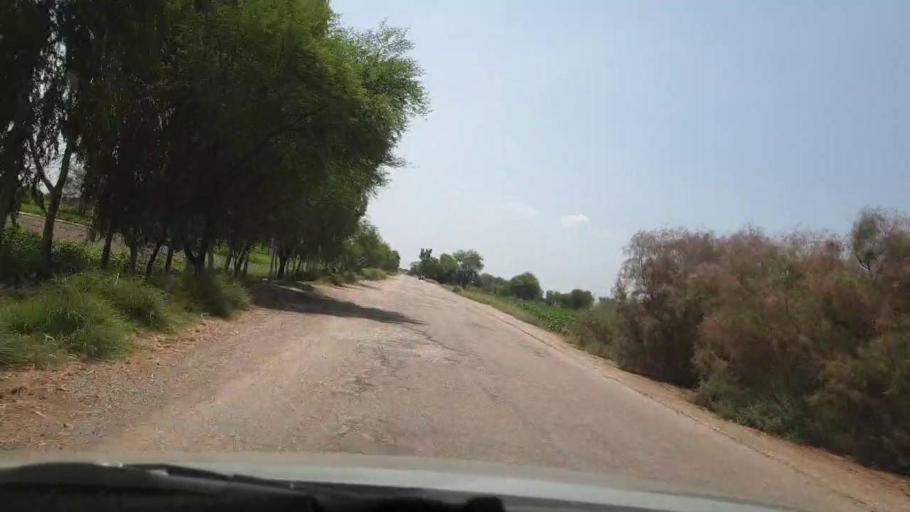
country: PK
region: Sindh
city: Rohri
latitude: 27.6695
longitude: 69.0584
